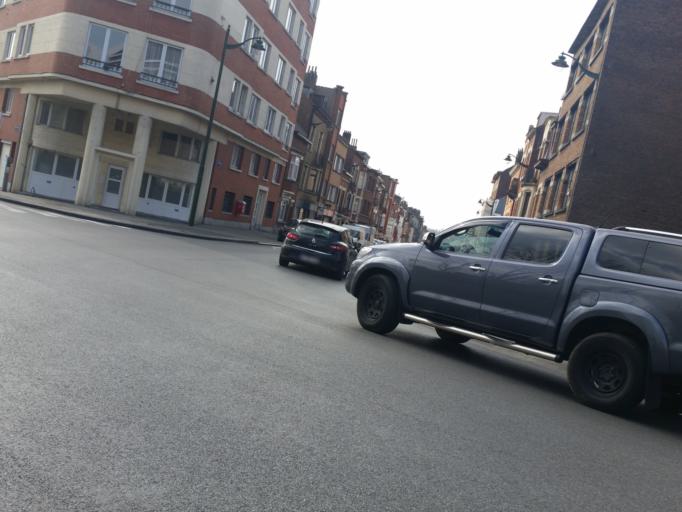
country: BE
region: Brussels Capital
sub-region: Bruxelles-Capitale
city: Brussels
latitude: 50.8416
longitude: 4.3158
